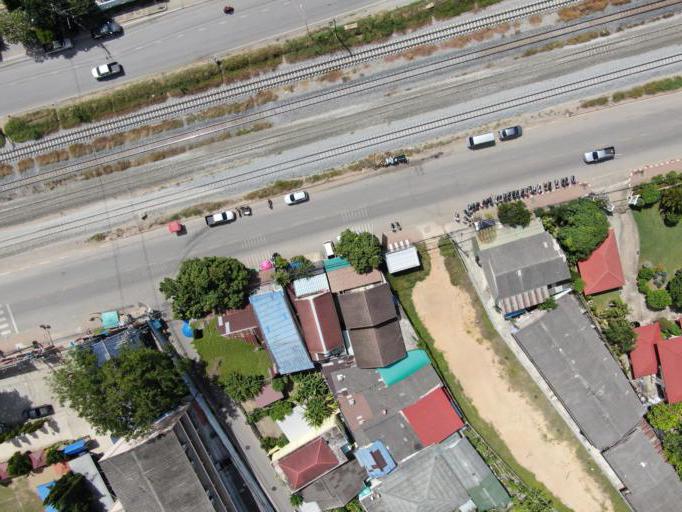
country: TH
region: Ratchaburi
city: Ban Pong
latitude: 13.8070
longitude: 99.8739
